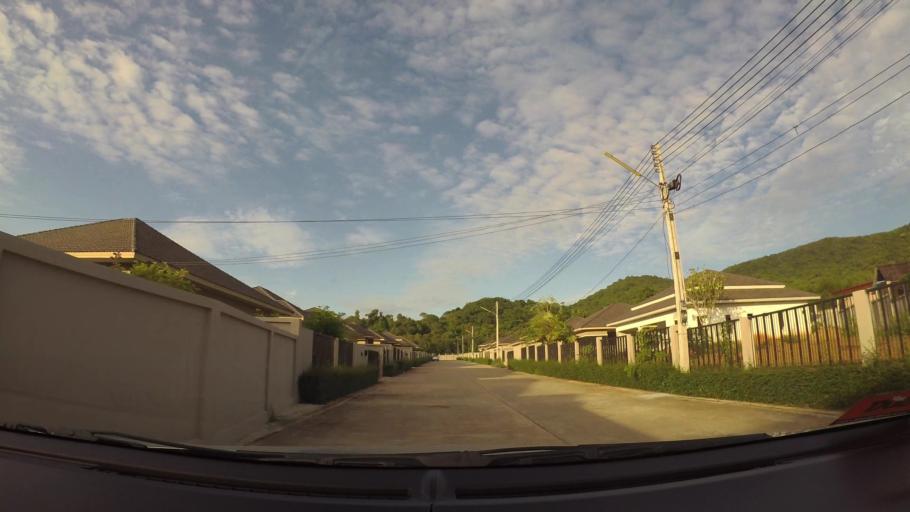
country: TH
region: Chon Buri
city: Sattahip
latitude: 12.7258
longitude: 100.9180
